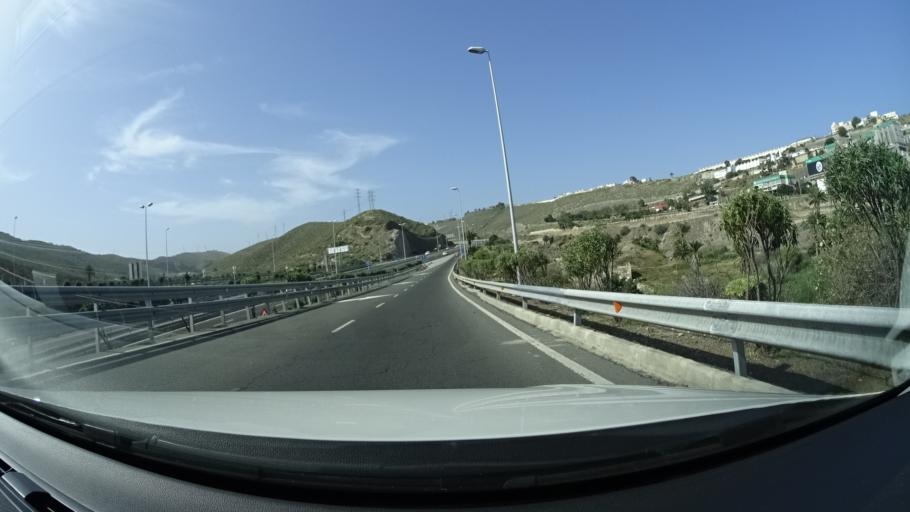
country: ES
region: Canary Islands
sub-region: Provincia de Las Palmas
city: Las Palmas de Gran Canaria
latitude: 28.0849
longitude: -15.4300
